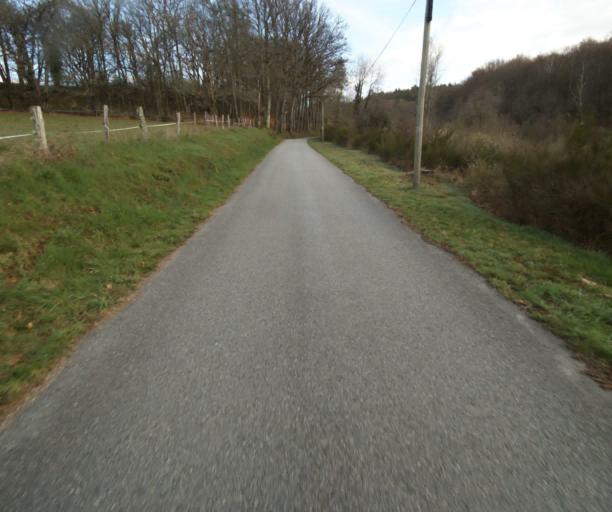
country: FR
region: Limousin
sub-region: Departement de la Correze
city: Correze
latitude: 45.3779
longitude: 1.8796
